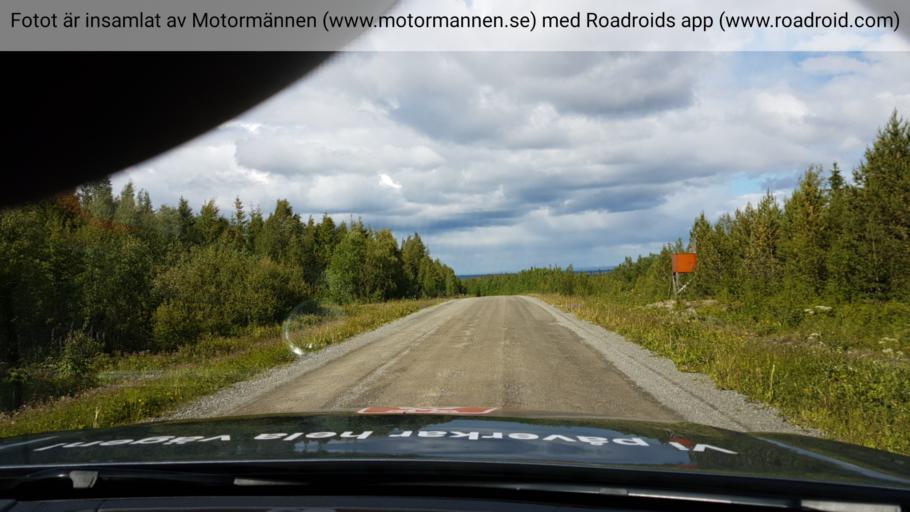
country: SE
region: Jaemtland
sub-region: Krokoms Kommun
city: Valla
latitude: 63.0488
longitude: 13.9614
